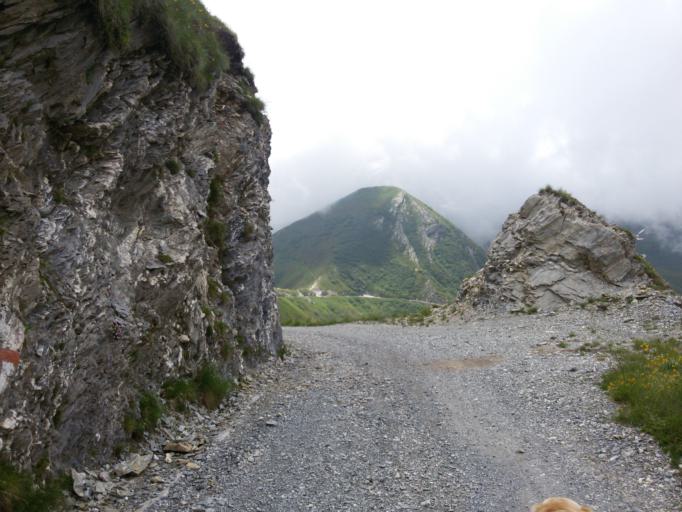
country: IT
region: Piedmont
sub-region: Provincia di Cuneo
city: Limone Piemonte
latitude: 44.1606
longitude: 7.6264
